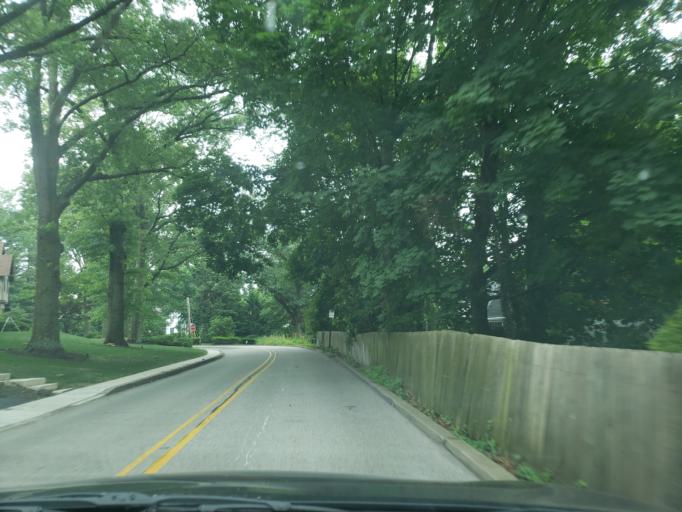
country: US
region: Pennsylvania
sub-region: Allegheny County
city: Ben Avon
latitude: 40.5130
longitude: -80.0729
